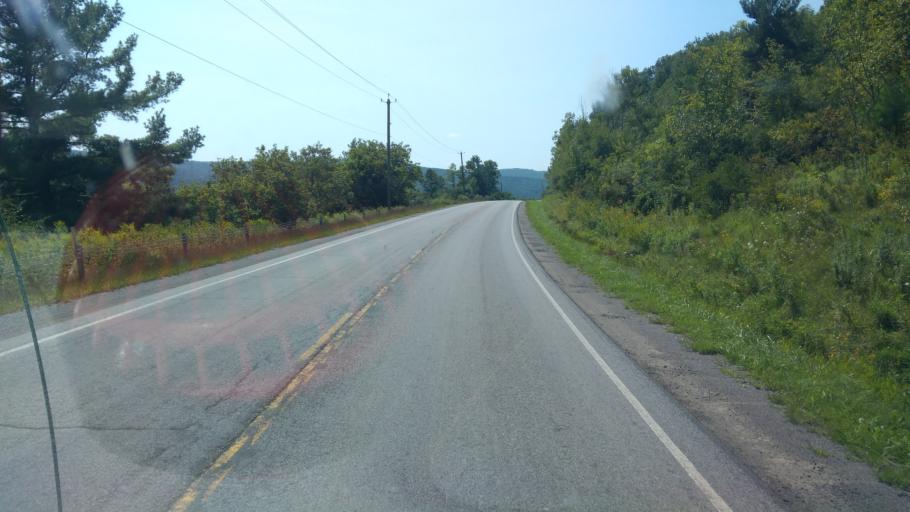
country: US
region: New York
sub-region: Allegany County
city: Belmont
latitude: 42.3124
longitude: -77.9551
